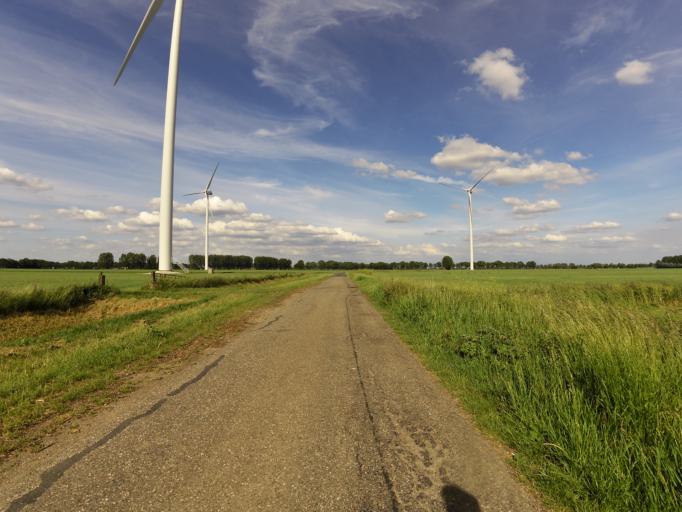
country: NL
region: Gelderland
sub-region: Gemeente Duiven
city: Duiven
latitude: 51.9744
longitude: 6.0158
